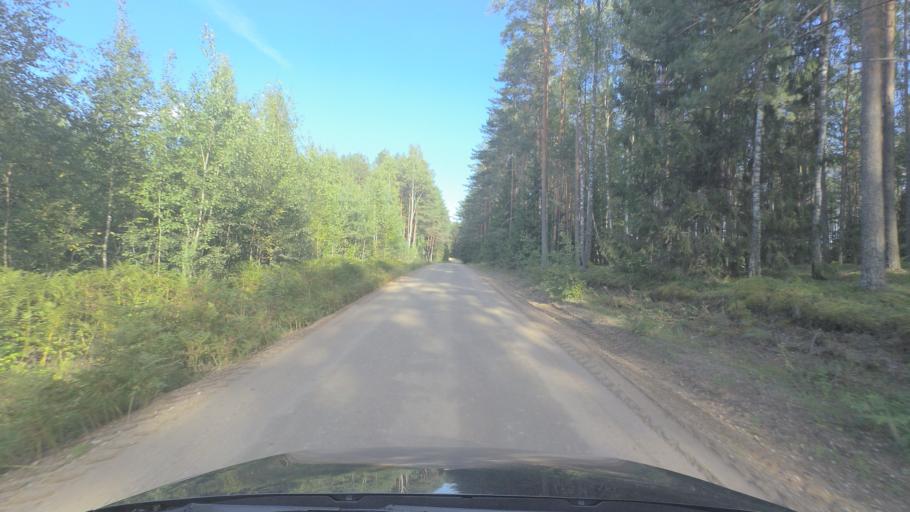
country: LT
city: Pabrade
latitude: 55.1620
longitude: 25.8205
